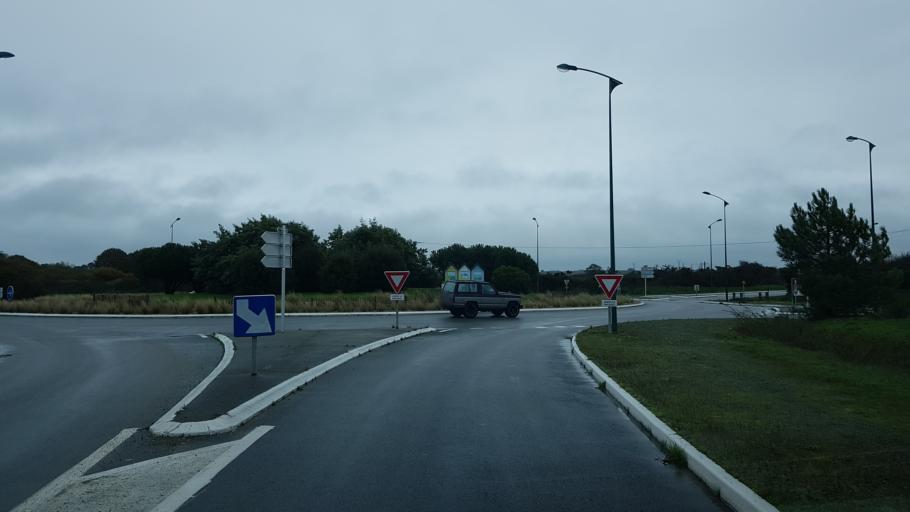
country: FR
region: Brittany
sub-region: Departement du Morbihan
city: Saint-Gildas-de-Rhuys
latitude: 47.5321
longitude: -2.8456
